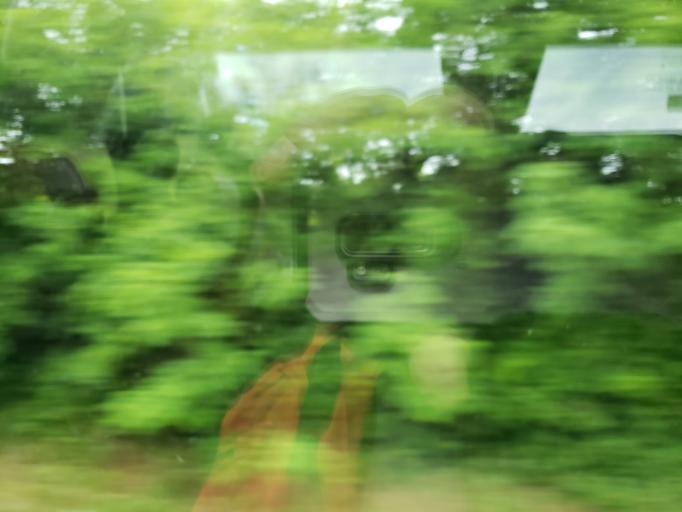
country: FR
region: Bourgogne
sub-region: Departement de l'Yonne
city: Venoy
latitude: 47.8104
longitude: 3.6797
